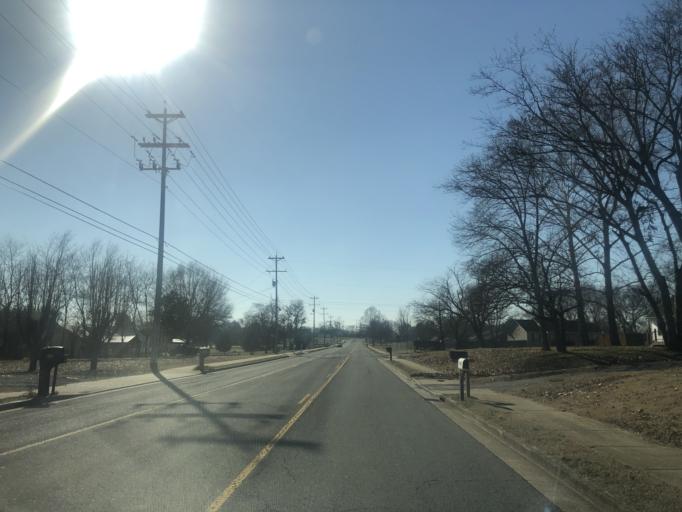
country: US
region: Tennessee
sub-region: Rutherford County
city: Smyrna
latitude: 35.9022
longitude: -86.4752
